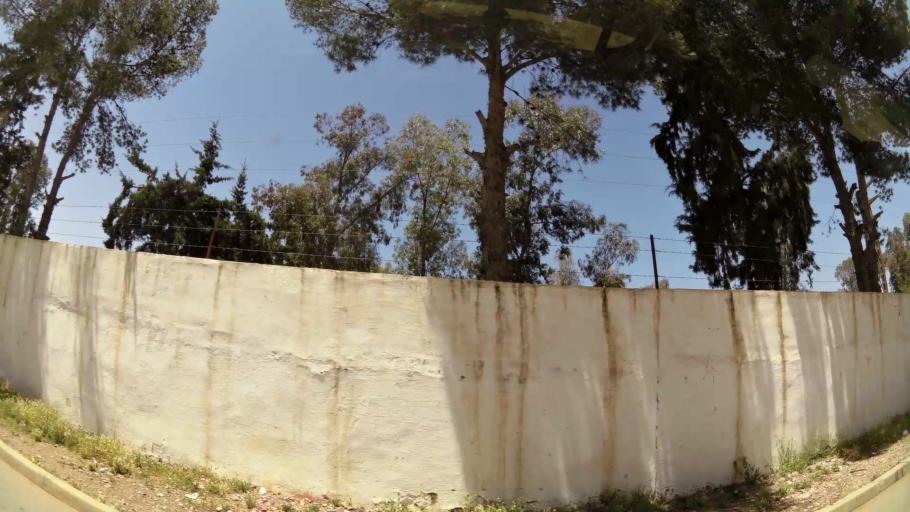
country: MA
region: Rabat-Sale-Zemmour-Zaer
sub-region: Khemisset
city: Khemisset
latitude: 33.8297
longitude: -6.0914
